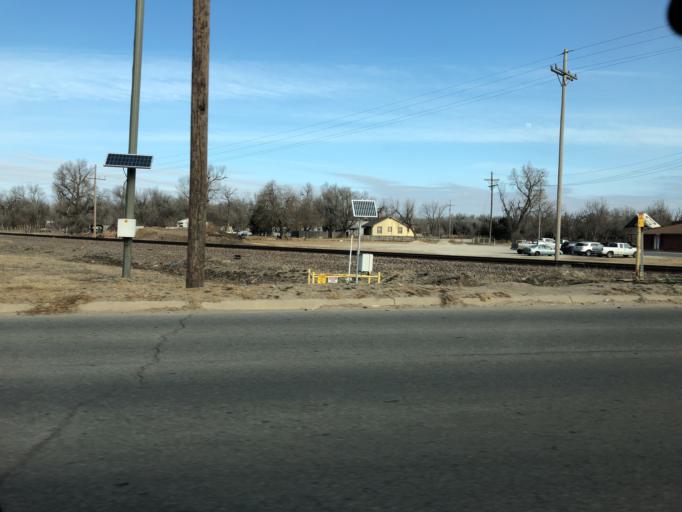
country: US
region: Kansas
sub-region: Reno County
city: Hutchinson
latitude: 38.0571
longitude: -97.9551
